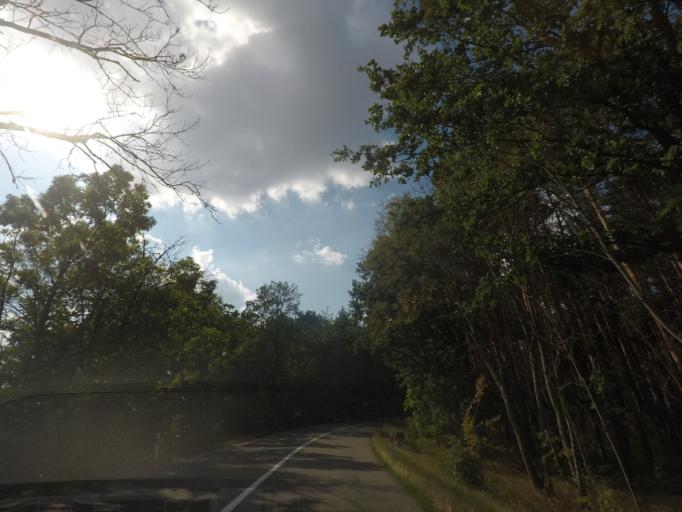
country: CZ
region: Kralovehradecky
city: Trebechovice pod Orebem
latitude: 50.2199
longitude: 15.9772
